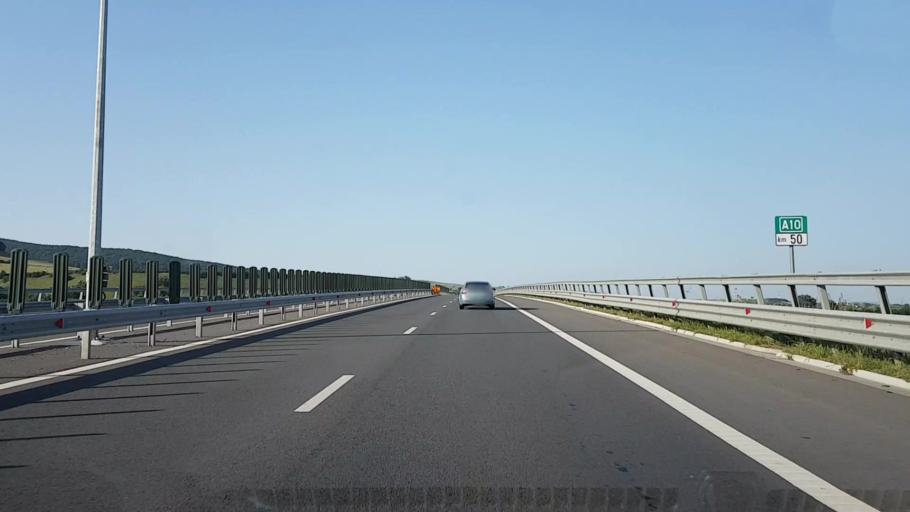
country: RO
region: Alba
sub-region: Comuna Miraslau
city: Miraslau
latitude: 46.3690
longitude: 23.7404
